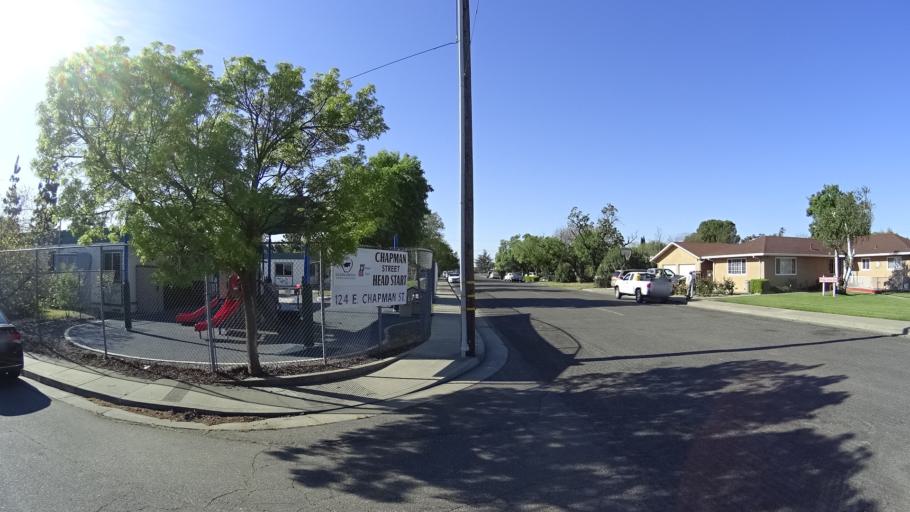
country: US
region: California
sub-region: Glenn County
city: Orland
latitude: 39.7416
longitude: -122.1845
